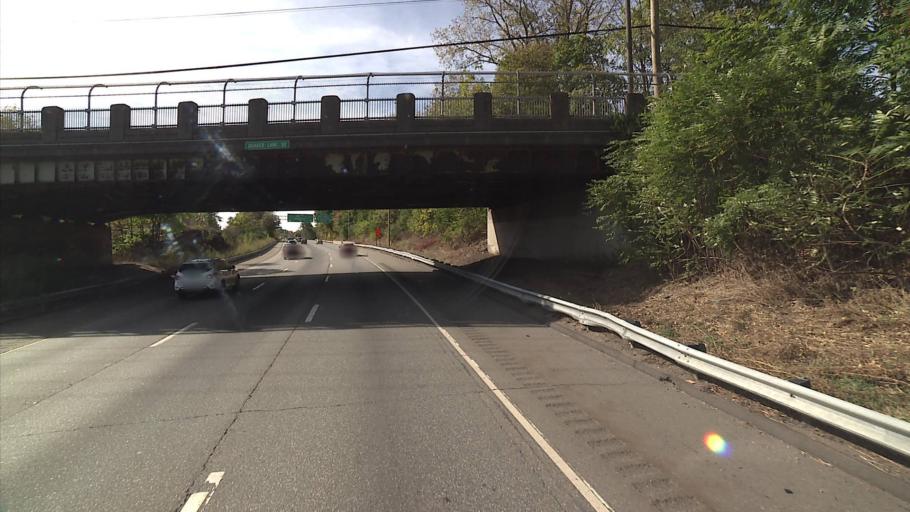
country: US
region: Connecticut
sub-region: Hartford County
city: West Hartford
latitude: 41.7502
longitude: -72.7290
